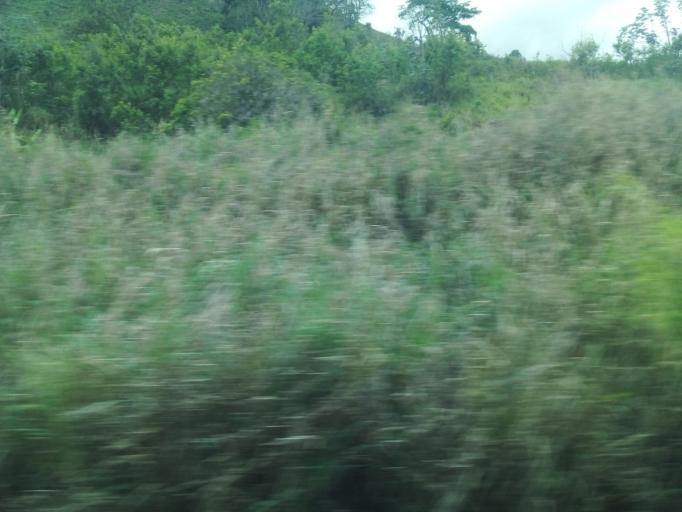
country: BR
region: Minas Gerais
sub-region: Timoteo
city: Timoteo
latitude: -19.5397
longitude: -42.6805
